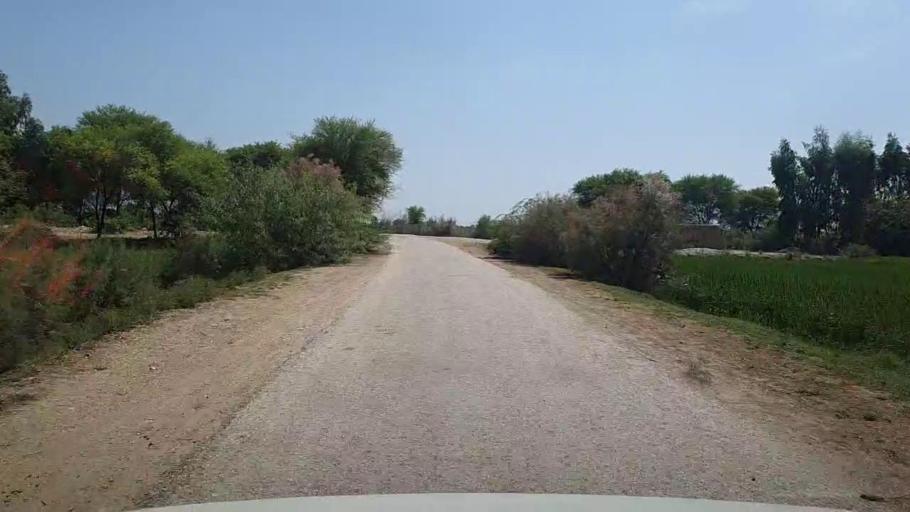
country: PK
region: Sindh
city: Kandhkot
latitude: 28.2927
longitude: 69.3514
